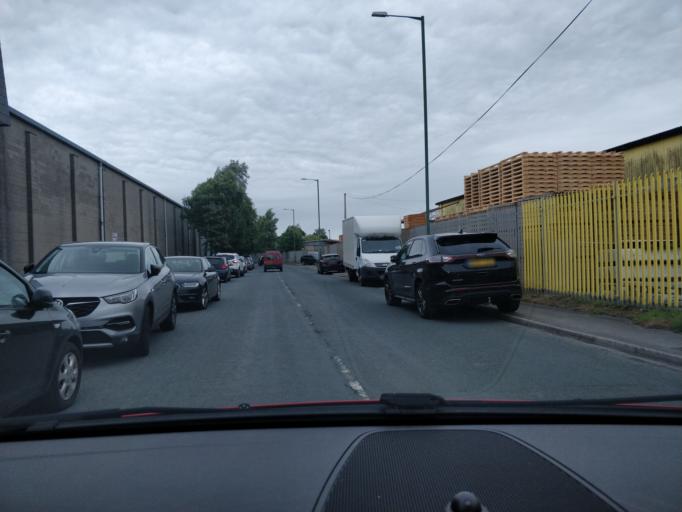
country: GB
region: England
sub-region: Lancashire
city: Ormskirk
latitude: 53.6009
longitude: -2.8655
